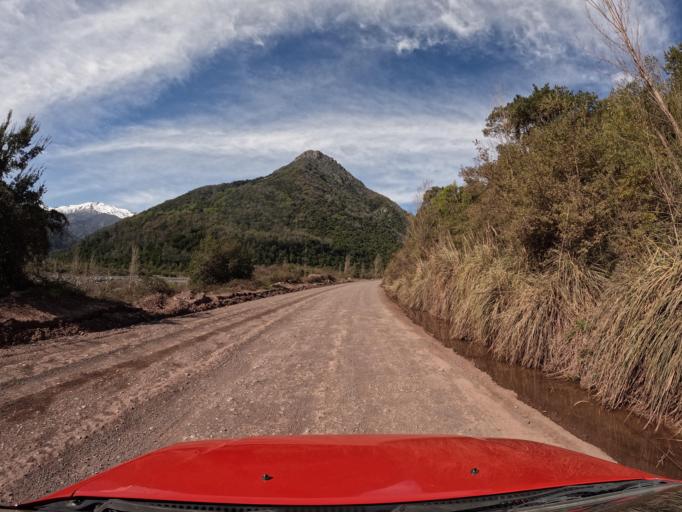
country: CL
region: O'Higgins
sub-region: Provincia de Colchagua
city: Chimbarongo
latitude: -35.0012
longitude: -70.7632
